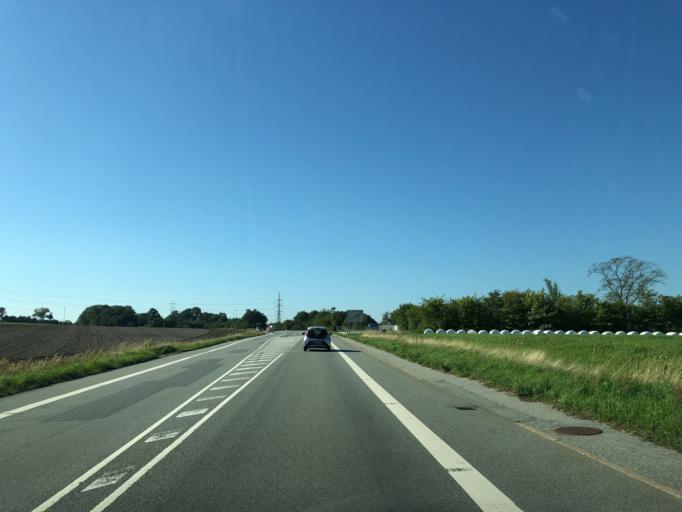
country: DK
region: South Denmark
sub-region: Aabenraa Kommune
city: Aabenraa
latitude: 55.0168
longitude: 9.4424
